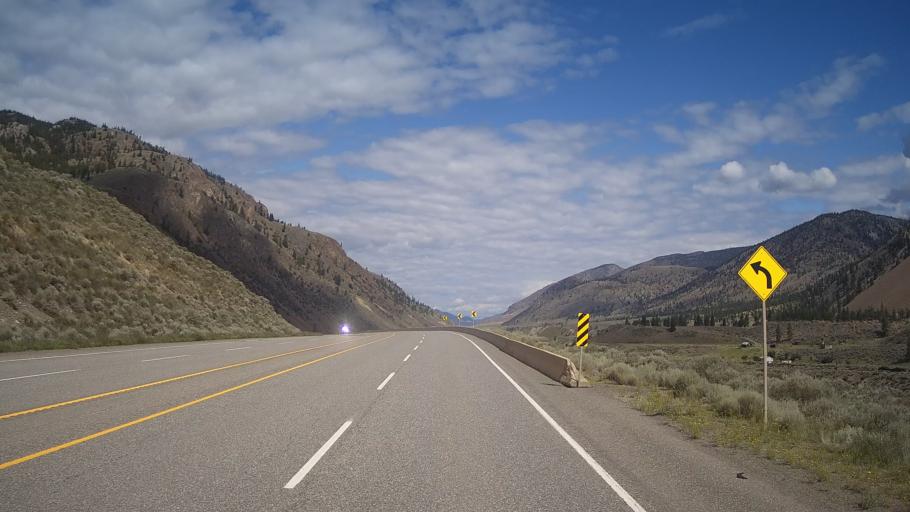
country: CA
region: British Columbia
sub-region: Thompson-Nicola Regional District
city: Ashcroft
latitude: 50.5154
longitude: -121.2816
